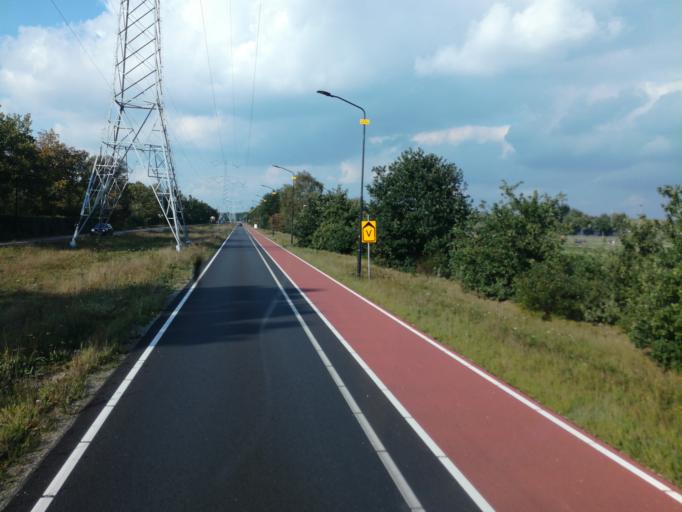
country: NL
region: North Brabant
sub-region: Gemeente Uden
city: Uden
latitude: 51.6673
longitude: 5.6426
